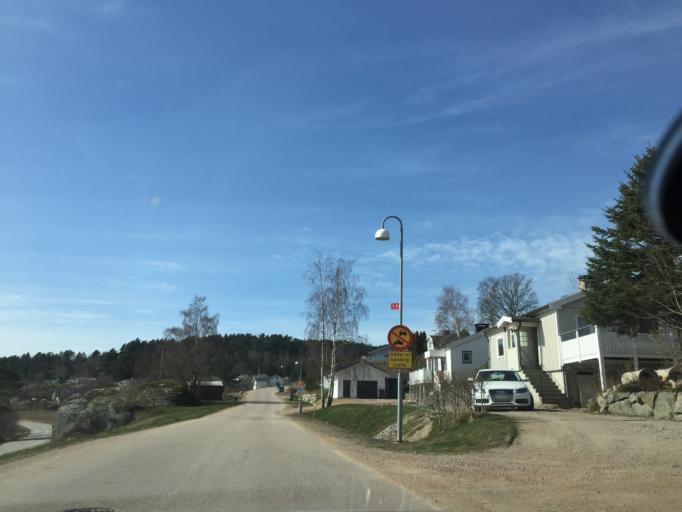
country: SE
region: Vaestra Goetaland
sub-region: Orust
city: Henan
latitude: 58.3427
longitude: 11.7368
